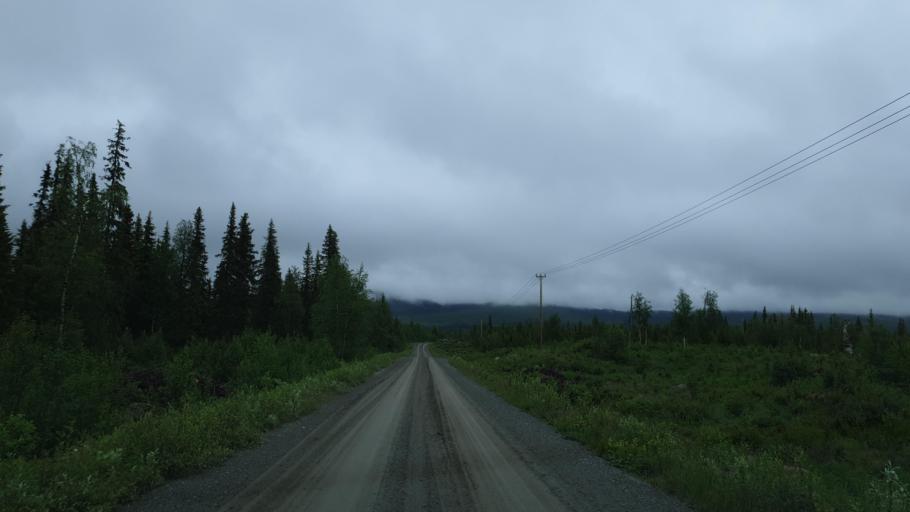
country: SE
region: Vaesterbotten
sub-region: Vilhelmina Kommun
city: Sjoberg
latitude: 65.3110
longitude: 16.0171
